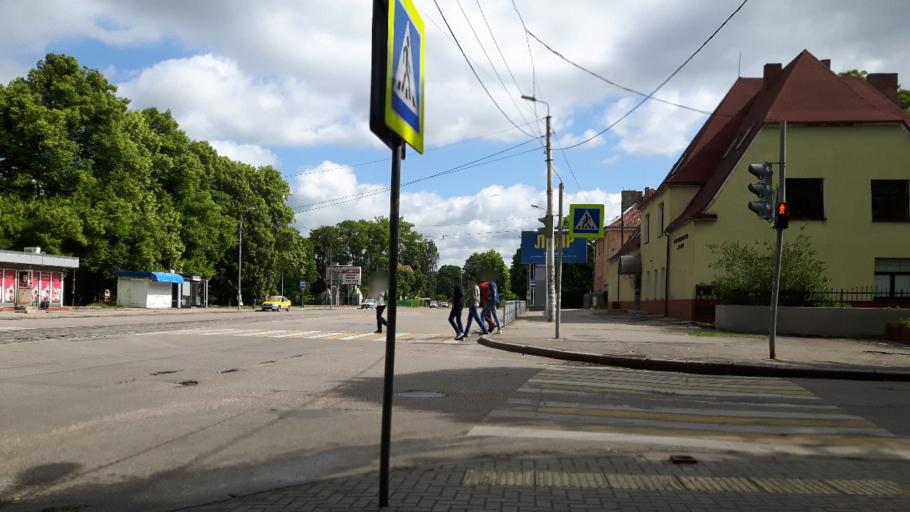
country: RU
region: Kaliningrad
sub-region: Gorod Kaliningrad
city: Kaliningrad
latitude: 54.7361
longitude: 20.5238
